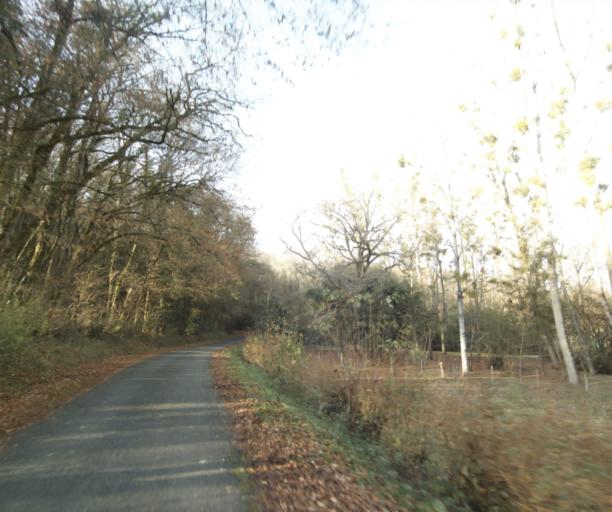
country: FR
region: Poitou-Charentes
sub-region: Departement de la Charente-Maritime
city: Chaniers
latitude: 45.7303
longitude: -0.5372
